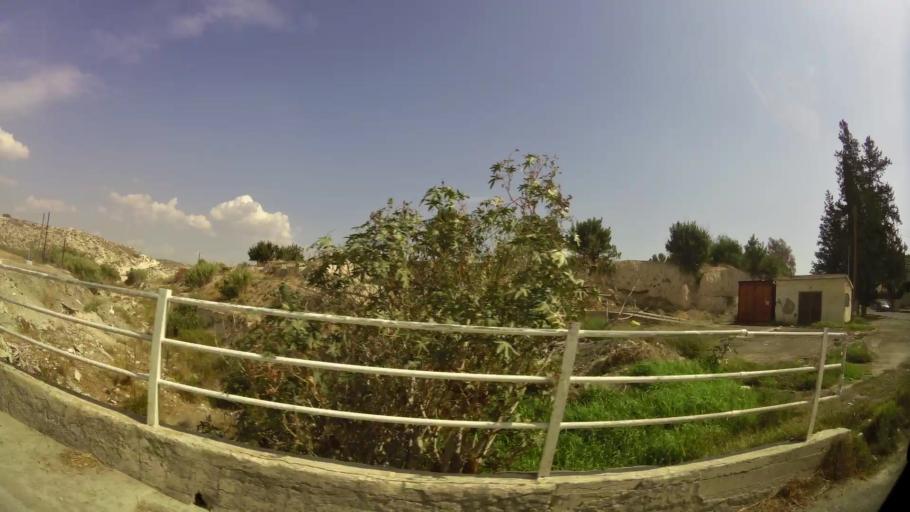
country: CY
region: Larnaka
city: Aradippou
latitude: 34.9529
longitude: 33.5823
